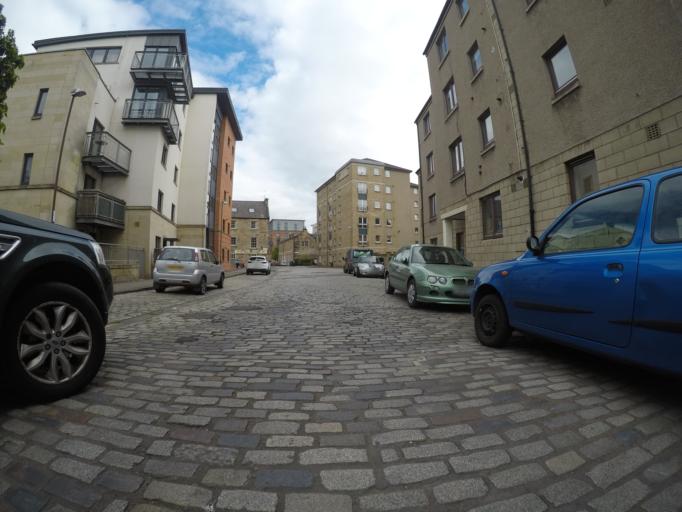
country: GB
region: Scotland
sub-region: West Lothian
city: Seafield
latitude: 55.9732
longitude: -3.1651
